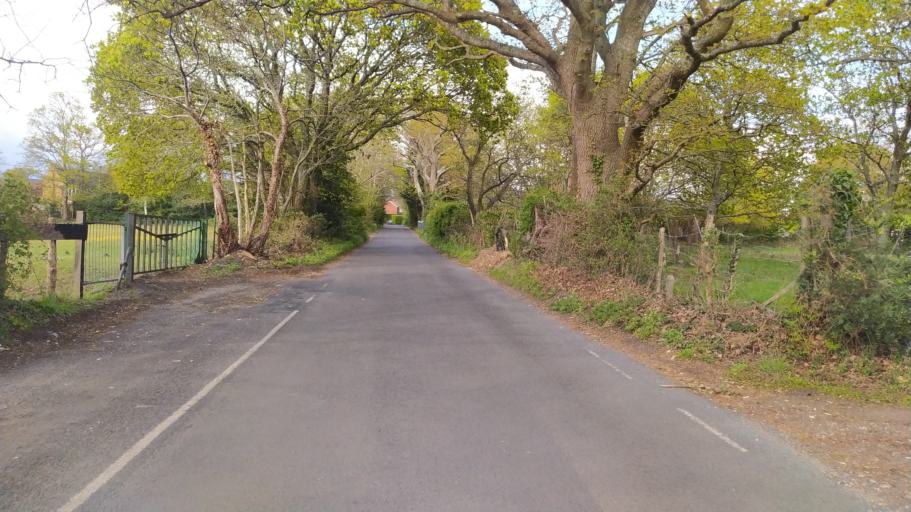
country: GB
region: England
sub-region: Hampshire
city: Bursledon
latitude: 50.8977
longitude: -1.3319
